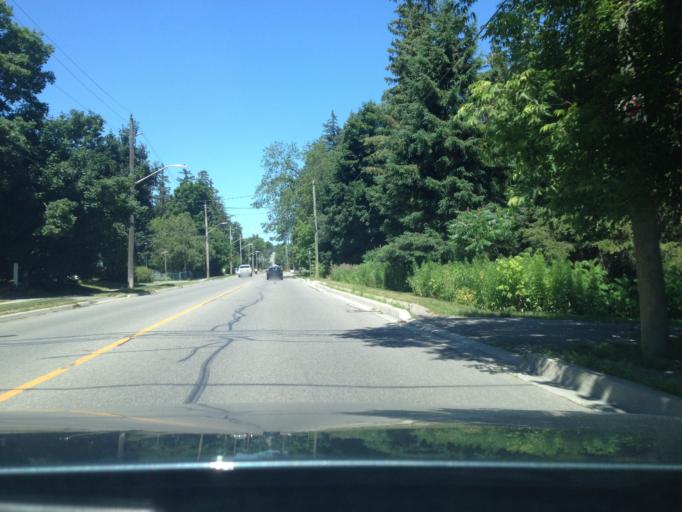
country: CA
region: Ontario
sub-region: Halton
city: Milton
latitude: 43.6644
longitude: -79.9223
